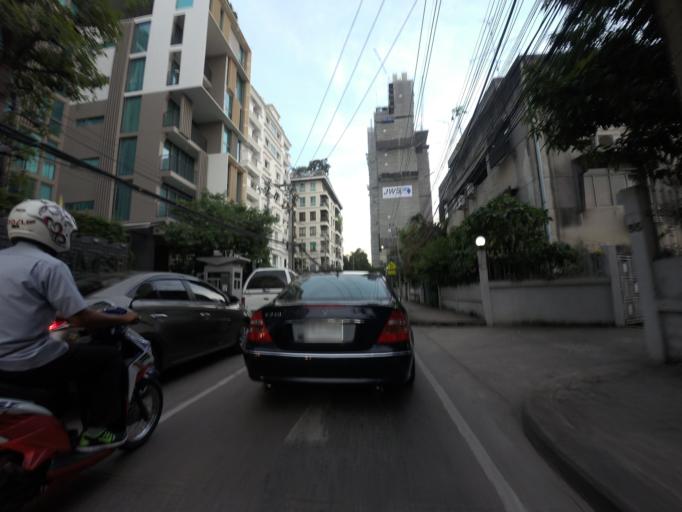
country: TH
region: Bangkok
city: Watthana
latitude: 13.7391
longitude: 100.5725
